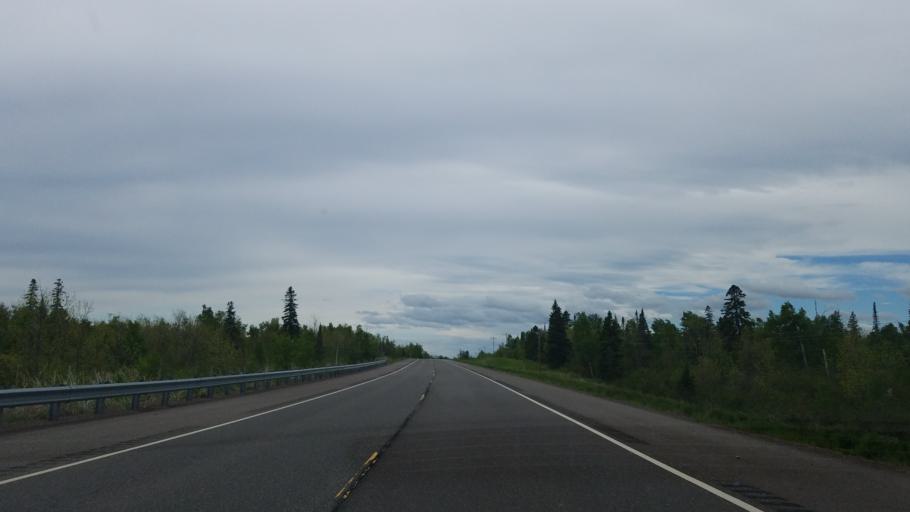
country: US
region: Minnesota
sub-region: Lake County
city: Silver Bay
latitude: 47.1971
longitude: -91.3852
